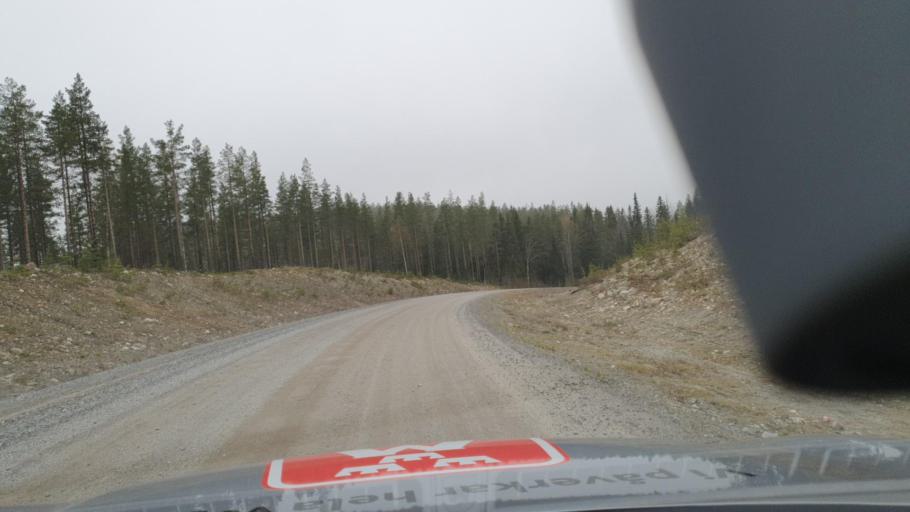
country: SE
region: Vaesternorrland
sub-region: OErnskoeldsviks Kommun
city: Husum
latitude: 63.6246
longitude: 19.0473
